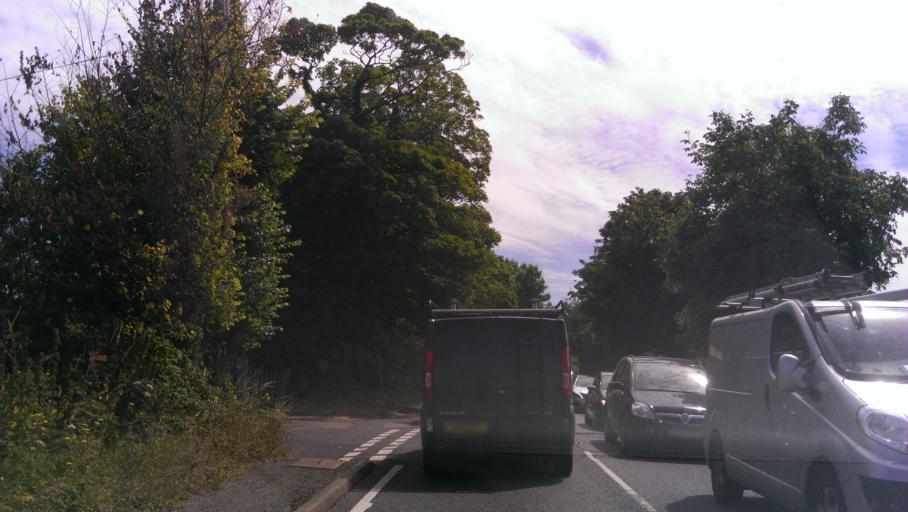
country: GB
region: England
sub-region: Kent
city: Faversham
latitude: 51.2958
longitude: 0.8896
